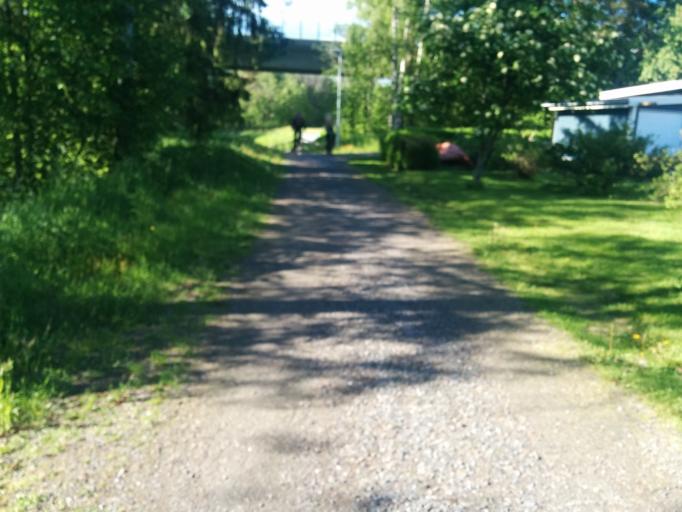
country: SE
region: Vaesterbotten
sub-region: Umea Kommun
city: Hoernefors
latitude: 63.6325
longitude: 19.9123
